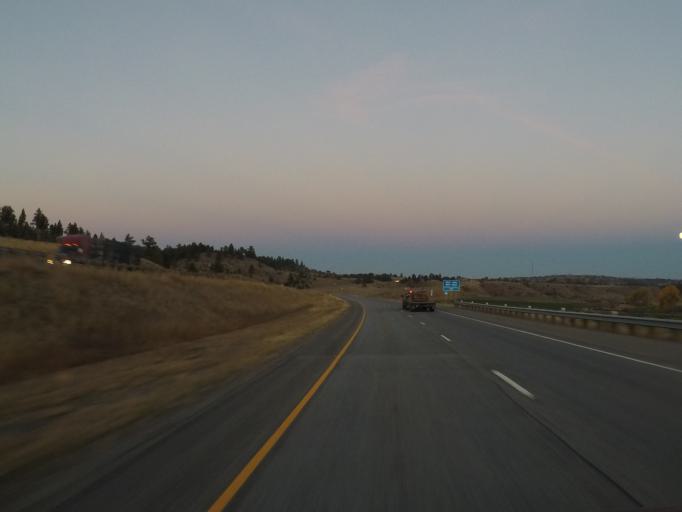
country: US
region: Montana
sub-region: Stillwater County
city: Columbus
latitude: 45.5957
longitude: -109.0835
